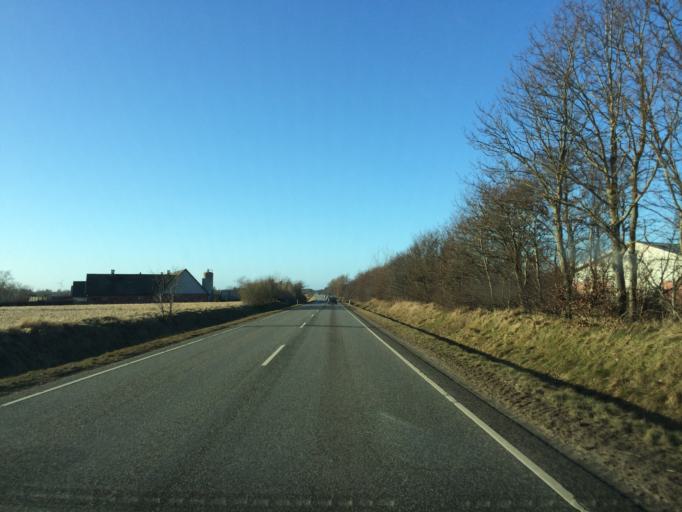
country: DK
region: Central Jutland
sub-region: Ringkobing-Skjern Kommune
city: Ringkobing
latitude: 56.1123
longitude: 8.3129
